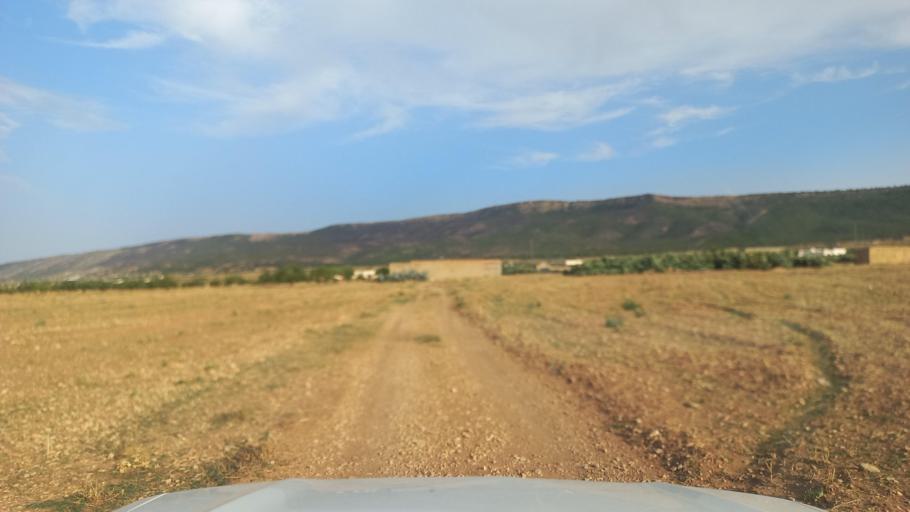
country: TN
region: Al Qasrayn
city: Kasserine
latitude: 35.3530
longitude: 8.8426
